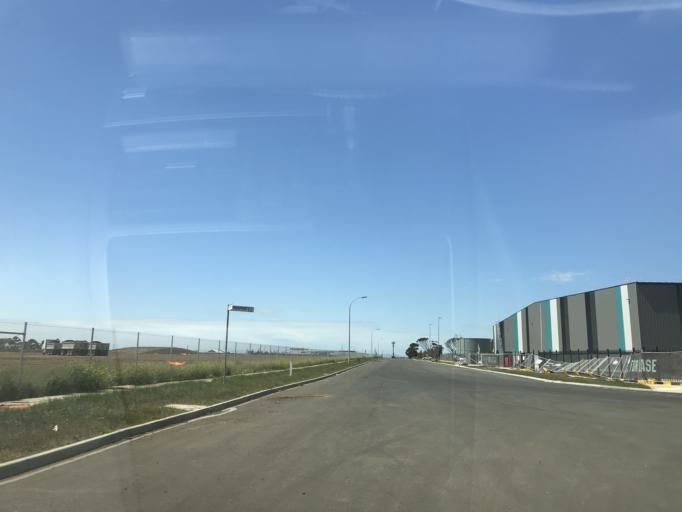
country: AU
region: Victoria
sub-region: Wyndham
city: Truganina
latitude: -37.8315
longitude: 144.7402
